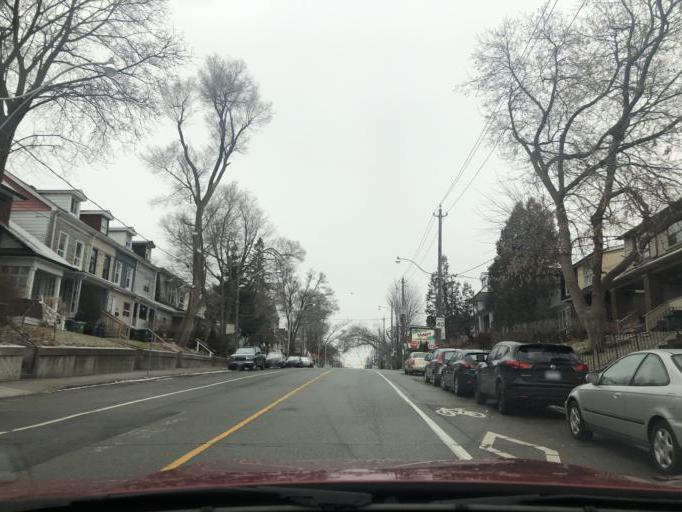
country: CA
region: Ontario
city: Toronto
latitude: 43.6743
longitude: -79.3378
